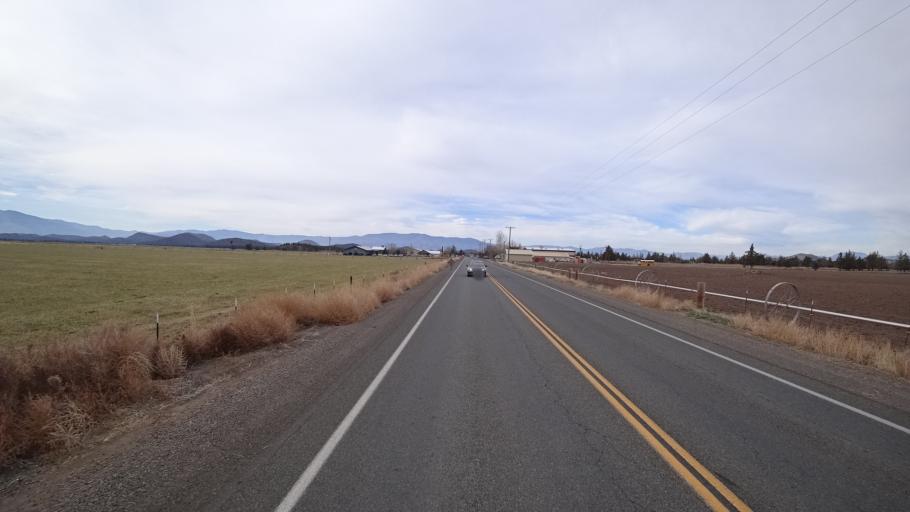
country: US
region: California
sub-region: Siskiyou County
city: Montague
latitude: 41.6239
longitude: -122.4024
